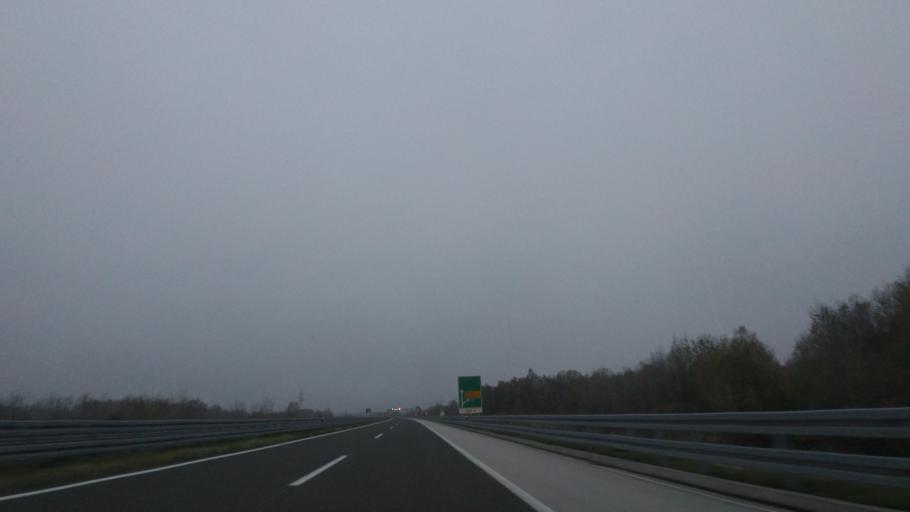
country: HR
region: Sisacko-Moslavacka
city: Lekenik
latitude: 45.5724
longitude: 16.2063
